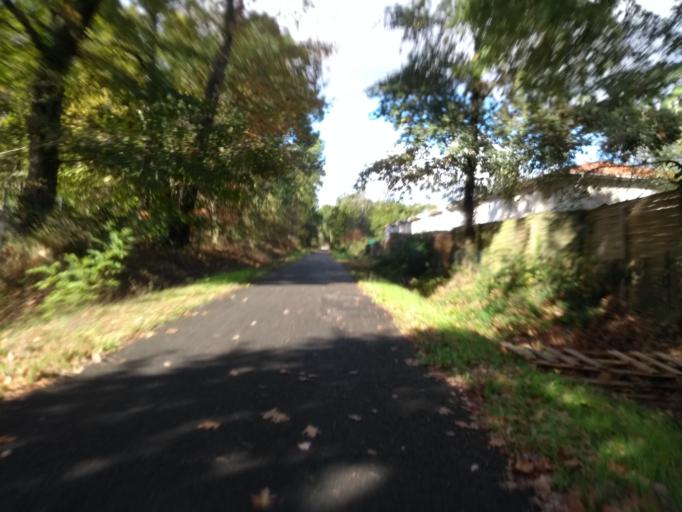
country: FR
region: Aquitaine
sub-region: Departement de la Gironde
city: Saint-Aubin-de-Medoc
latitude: 44.7819
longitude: -0.6944
